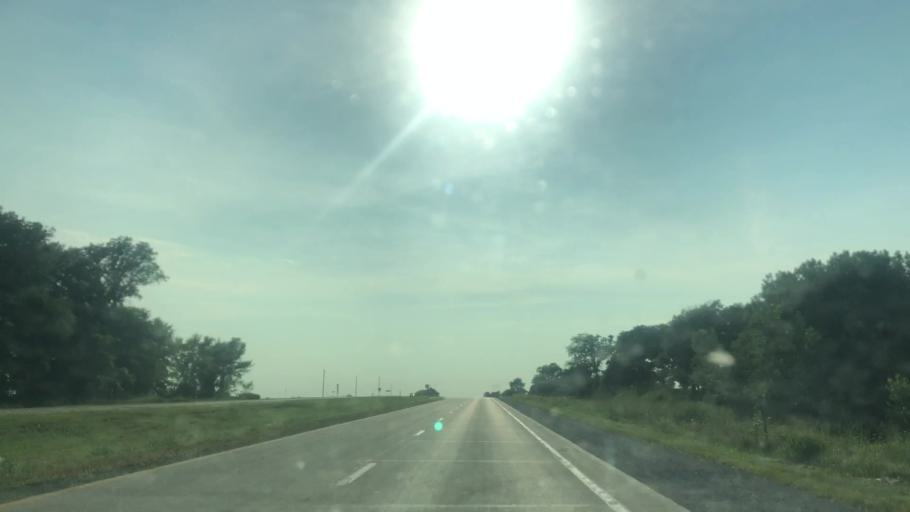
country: US
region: Iowa
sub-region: Story County
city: Nevada
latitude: 42.0078
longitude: -93.3884
